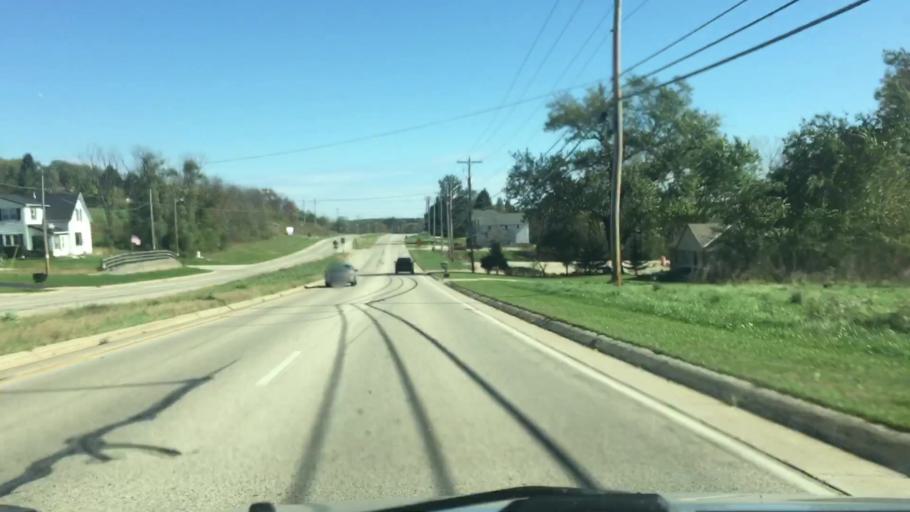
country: US
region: Wisconsin
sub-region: Waukesha County
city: Waukesha
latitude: 43.0138
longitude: -88.1910
